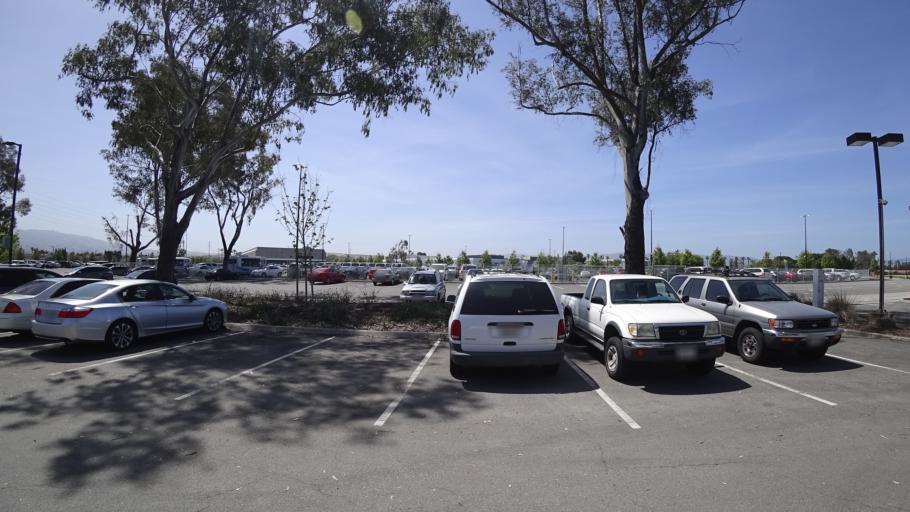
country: US
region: California
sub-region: Santa Clara County
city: Alum Rock
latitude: 37.3295
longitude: -121.8129
